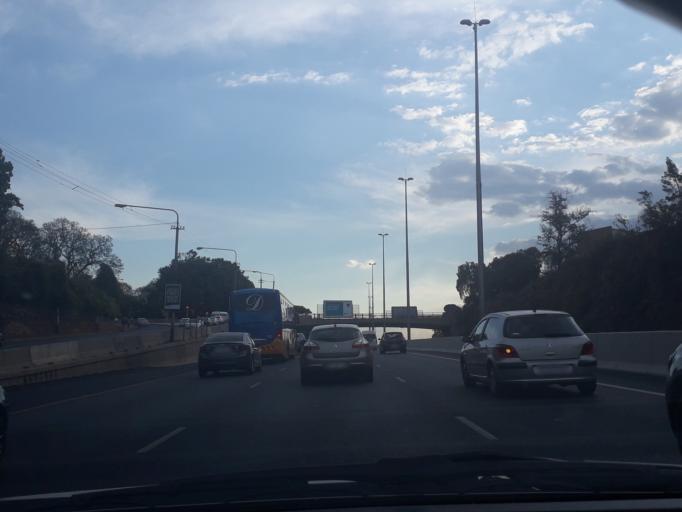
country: ZA
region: Gauteng
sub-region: City of Johannesburg Metropolitan Municipality
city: Johannesburg
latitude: -26.1774
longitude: 28.0375
